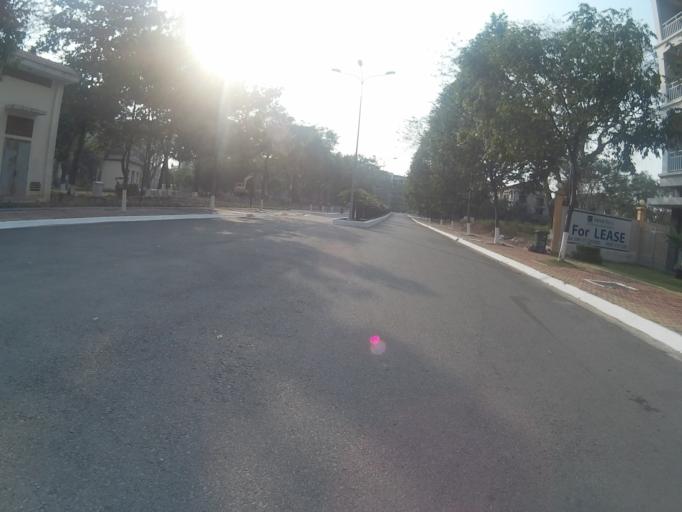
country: VN
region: Ho Chi Minh City
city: Ho Chi Minh City
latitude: 10.8555
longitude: 106.6273
